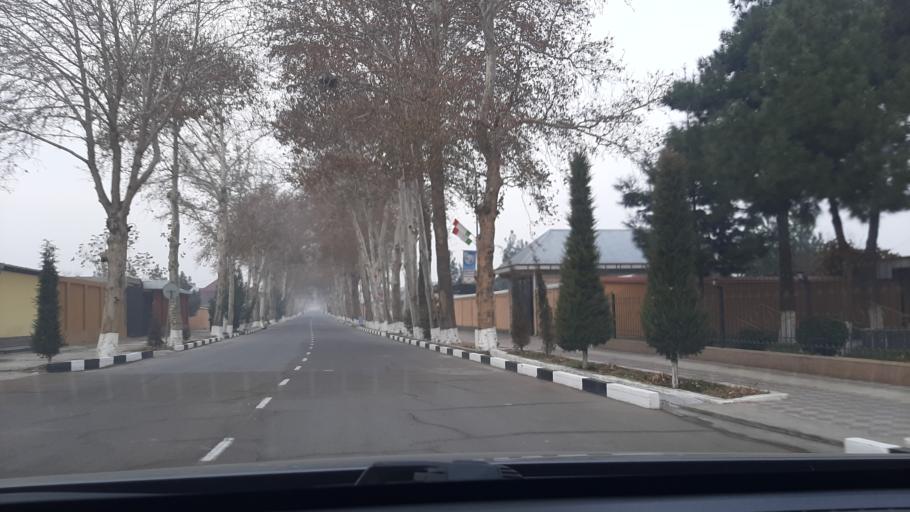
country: TJ
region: Viloyati Sughd
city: Chkalov
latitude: 40.2391
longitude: 69.7002
